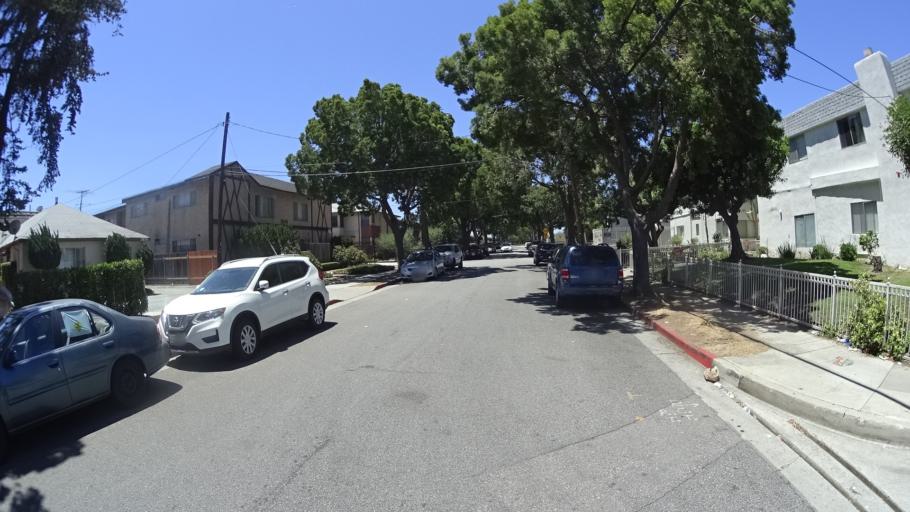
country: US
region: California
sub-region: Los Angeles County
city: Santa Monica
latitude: 34.0249
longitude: -118.4631
